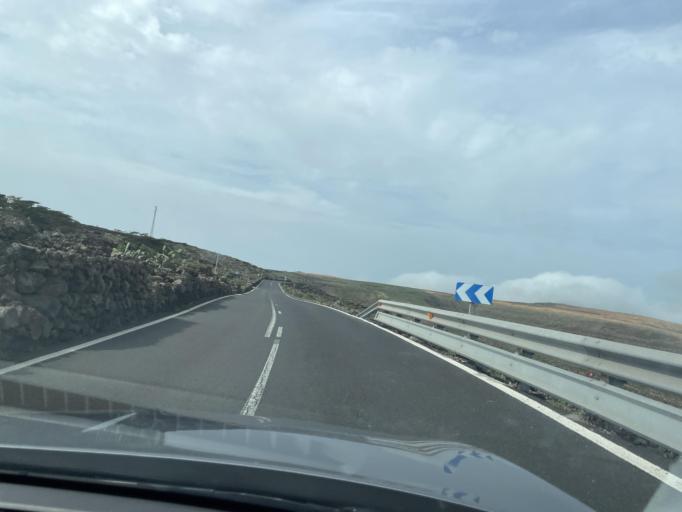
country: ES
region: Canary Islands
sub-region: Provincia de Las Palmas
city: Haria
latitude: 29.1933
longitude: -13.4737
